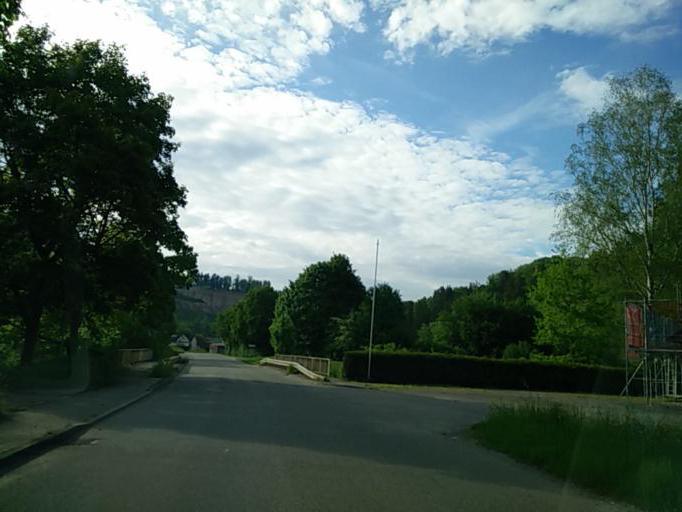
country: DE
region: Baden-Wuerttemberg
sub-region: Tuebingen Region
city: Hirrlingen
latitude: 48.4119
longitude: 8.8701
